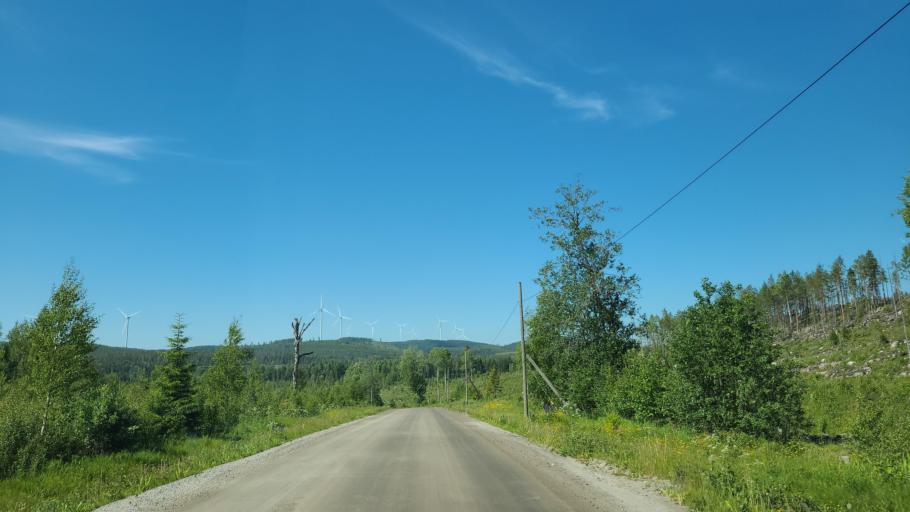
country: SE
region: Vaesterbotten
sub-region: Bjurholms Kommun
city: Bjurholm
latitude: 63.7045
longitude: 18.9118
